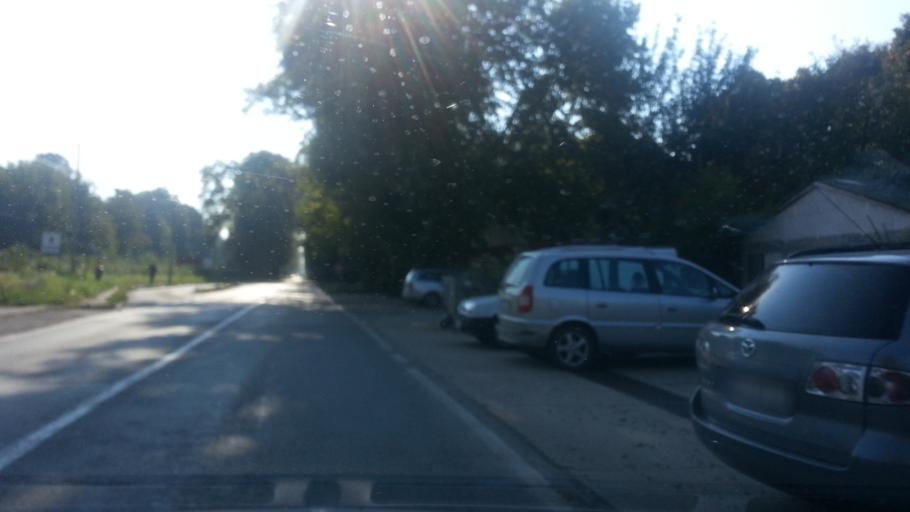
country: RS
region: Central Serbia
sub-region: Belgrade
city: Zemun
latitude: 44.8655
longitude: 20.3633
